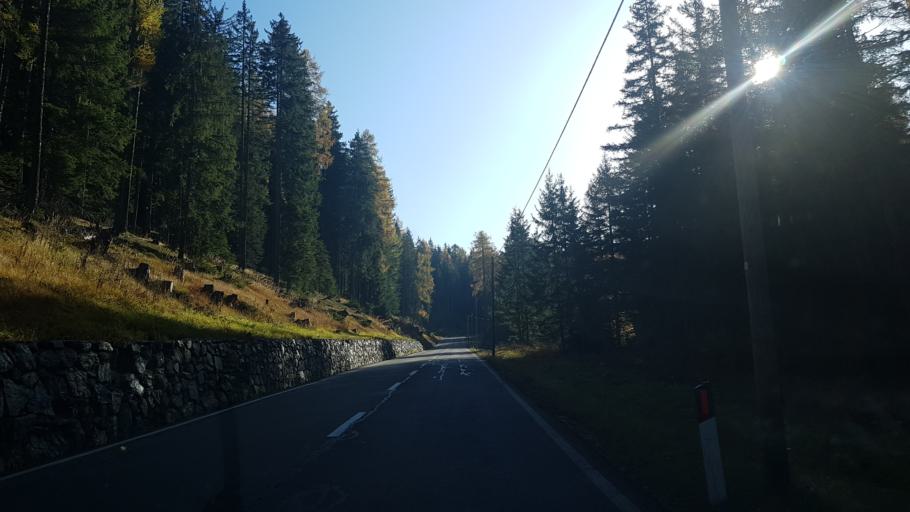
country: IT
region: Trentino-Alto Adige
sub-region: Bolzano
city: Sesto
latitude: 46.6836
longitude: 12.3737
